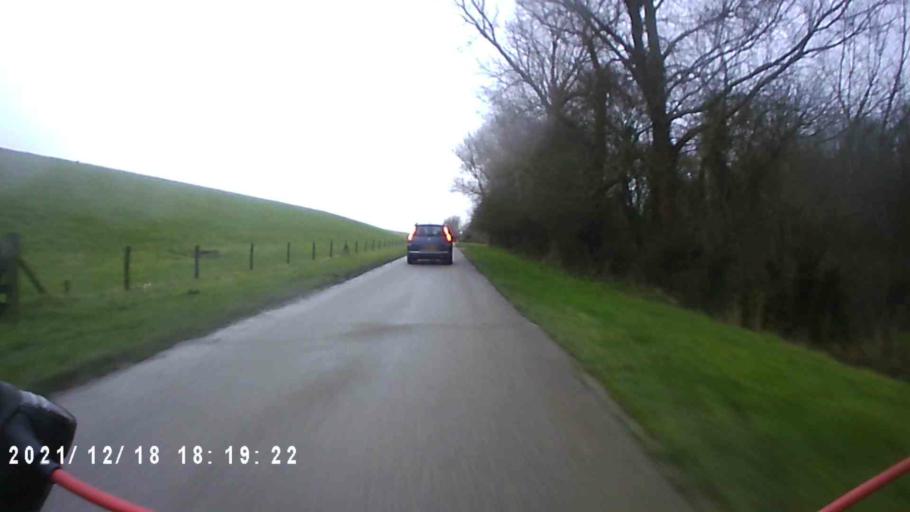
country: NL
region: Friesland
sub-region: Gemeente Dongeradeel
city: Ternaard
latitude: 53.3931
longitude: 5.9763
